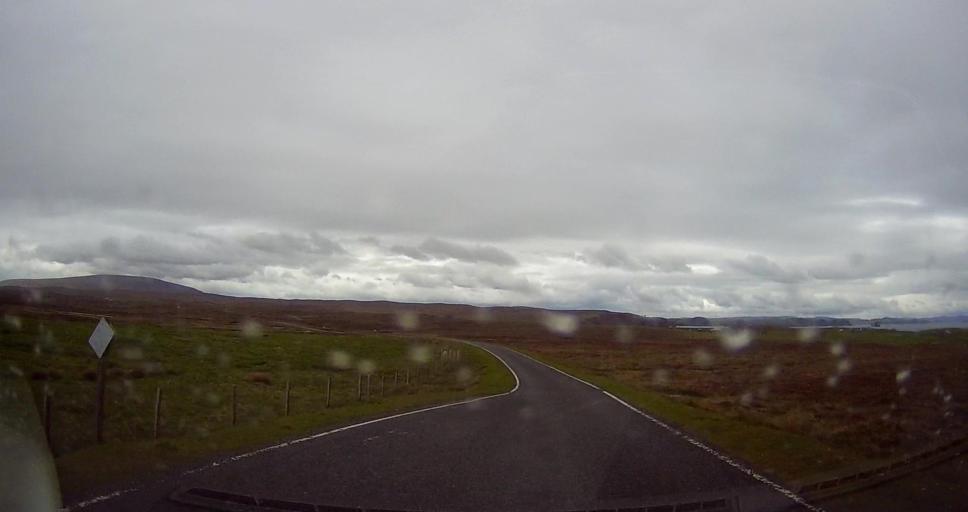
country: GB
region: Scotland
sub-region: Shetland Islands
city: Lerwick
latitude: 60.4892
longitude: -1.5920
